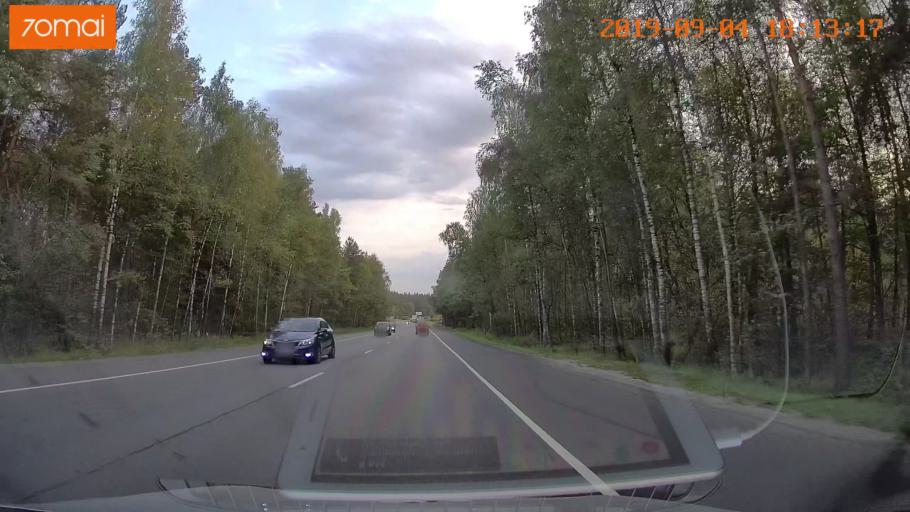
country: RU
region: Moskovskaya
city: Lopatinskiy
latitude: 55.3622
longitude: 38.7351
